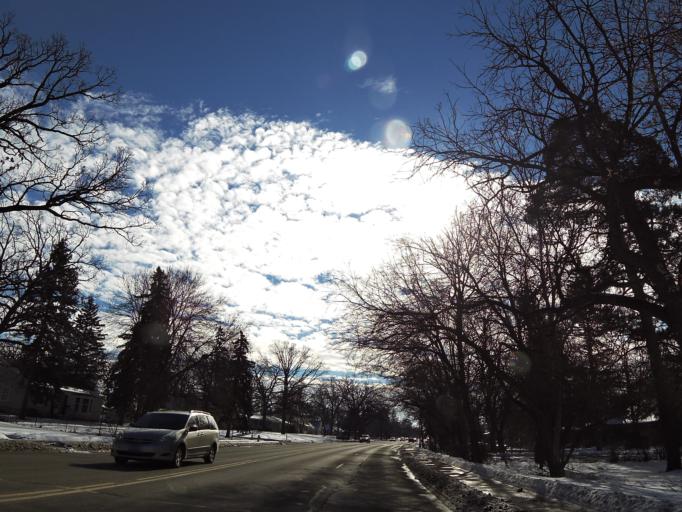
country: US
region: Minnesota
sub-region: Hennepin County
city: Richfield
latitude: 44.8734
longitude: -93.2886
